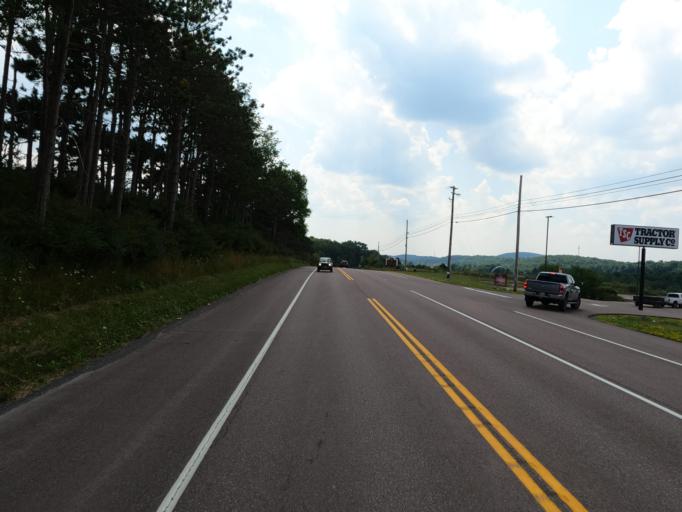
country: US
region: Maryland
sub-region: Garrett County
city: Oakland
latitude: 39.4313
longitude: -79.3856
